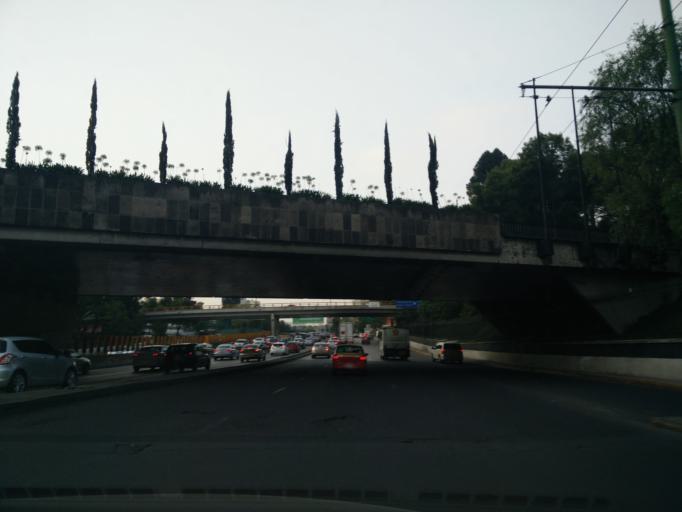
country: MX
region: Mexico City
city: Polanco
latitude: 19.4225
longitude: -99.1780
